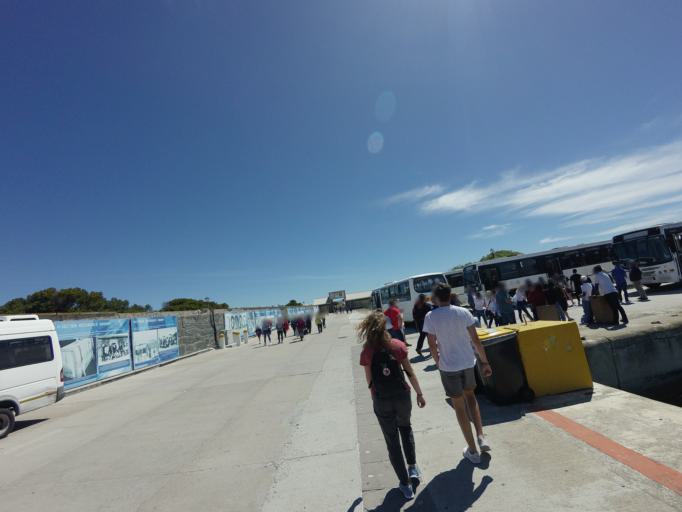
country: ZA
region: Western Cape
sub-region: City of Cape Town
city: Sunset Beach
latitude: -33.7989
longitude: 18.3758
